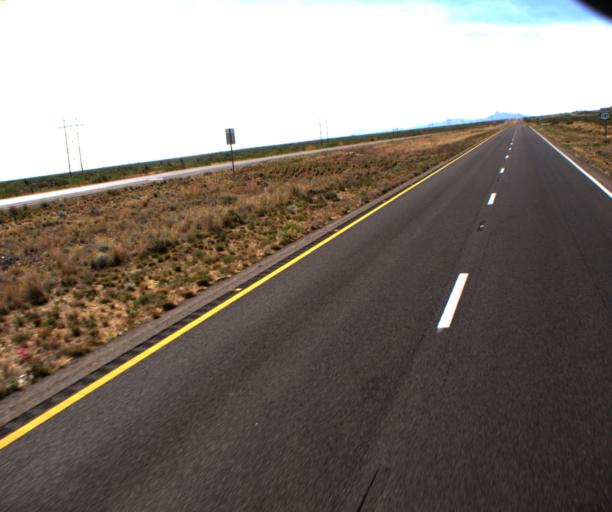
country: US
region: Arizona
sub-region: Graham County
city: Swift Trail Junction
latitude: 32.5550
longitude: -109.6785
